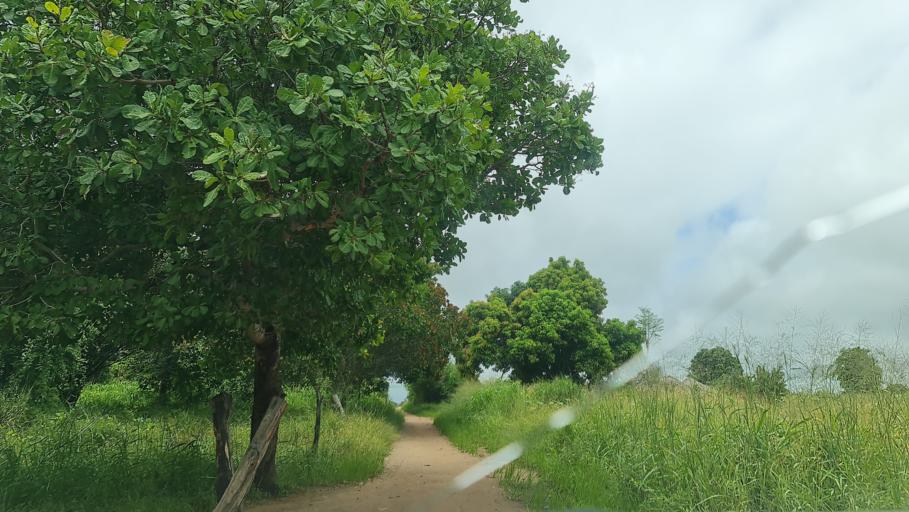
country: MW
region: Southern Region
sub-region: Nsanje District
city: Nsanje
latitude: -17.3369
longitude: 35.7186
